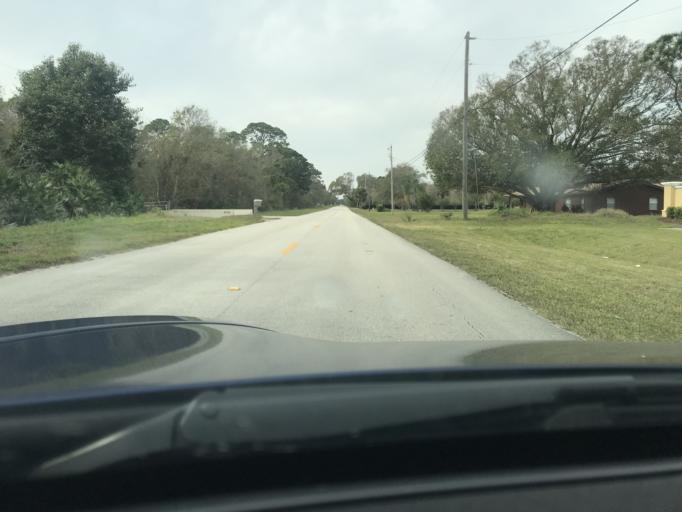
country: US
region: Florida
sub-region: Indian River County
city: Winter Beach
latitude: 27.7118
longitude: -80.4497
